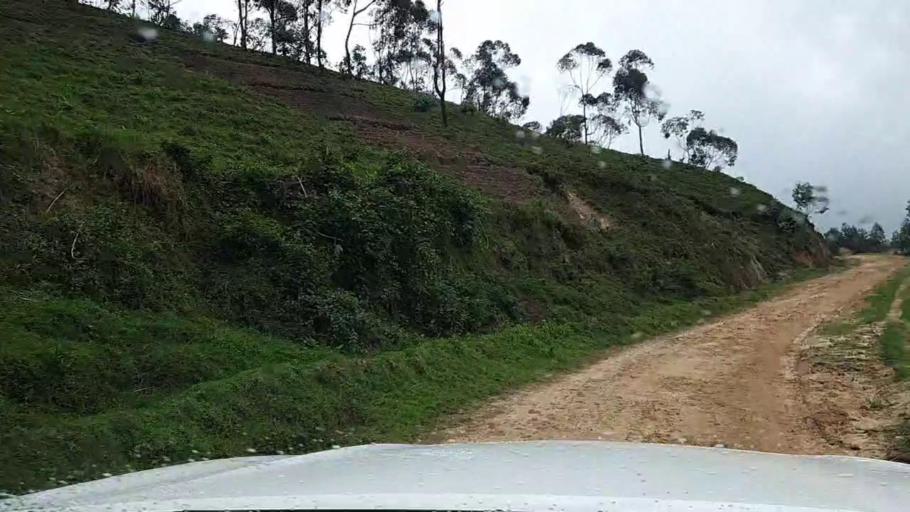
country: RW
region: Western Province
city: Kibuye
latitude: -2.2903
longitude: 29.3819
